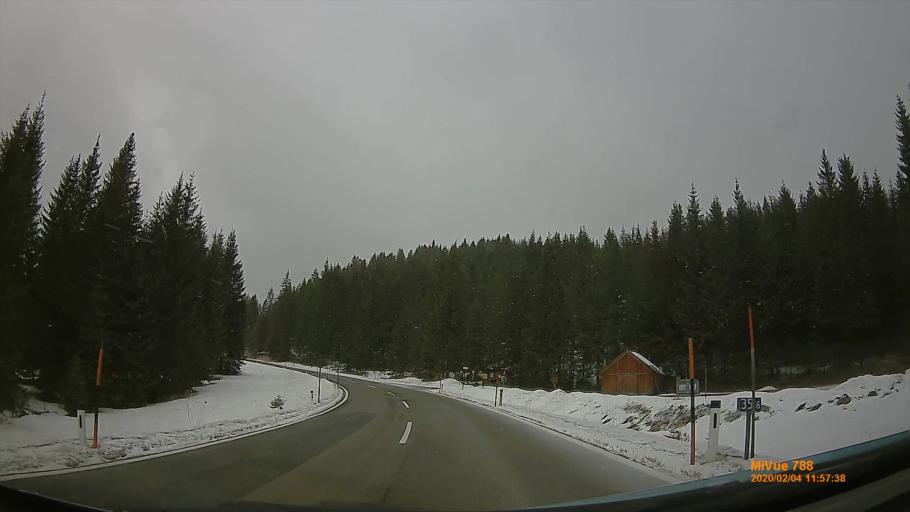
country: AT
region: Styria
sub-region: Politischer Bezirk Bruck-Muerzzuschlag
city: Muerzsteg
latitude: 47.7714
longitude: 15.5123
